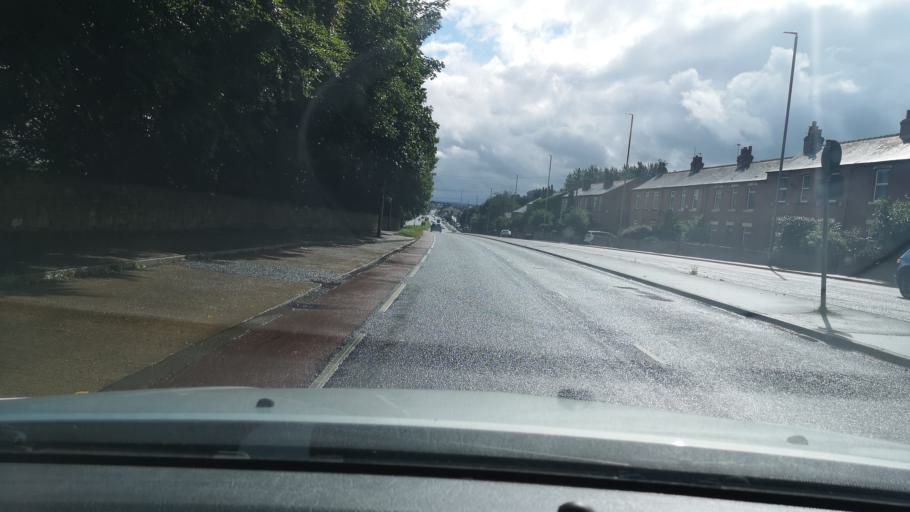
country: GB
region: England
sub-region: City and Borough of Leeds
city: Morley
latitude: 53.7207
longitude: -1.5905
